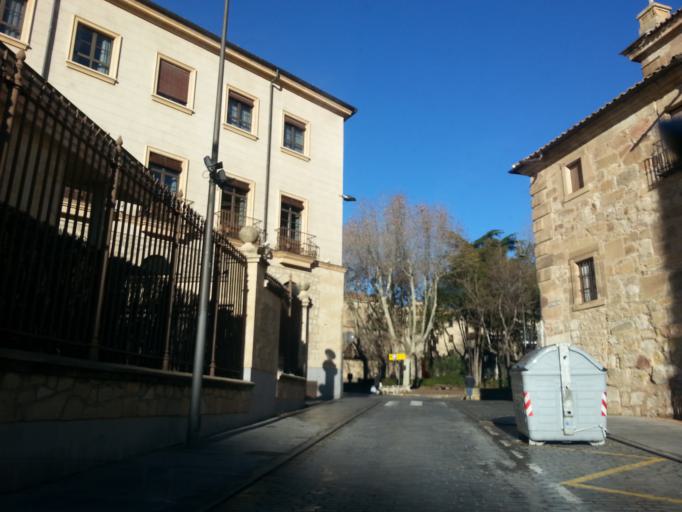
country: ES
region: Castille and Leon
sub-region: Provincia de Salamanca
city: Salamanca
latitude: 40.9617
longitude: -5.6636
